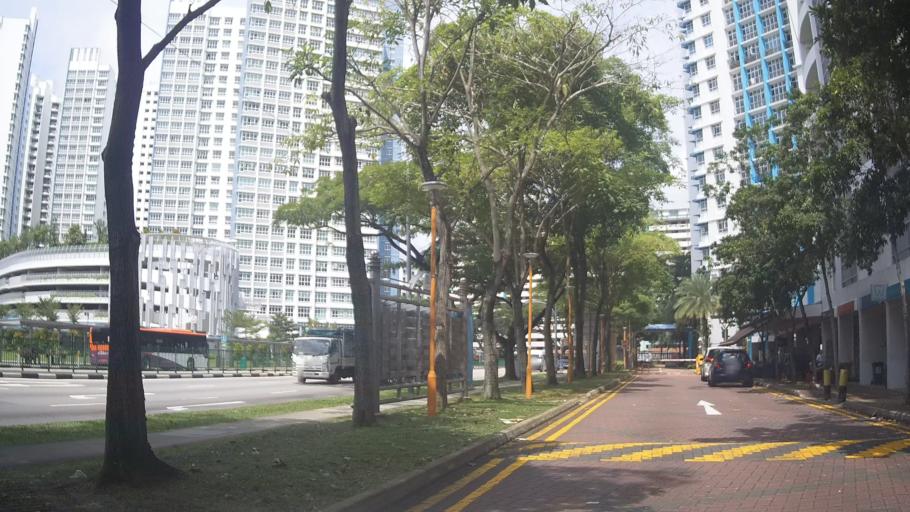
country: SG
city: Singapore
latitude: 1.3124
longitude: 103.8721
